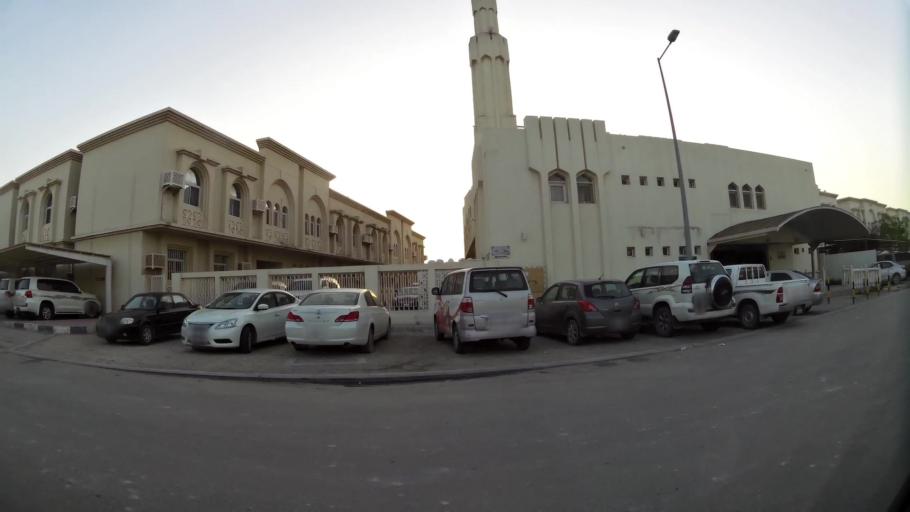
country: QA
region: Baladiyat ar Rayyan
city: Ar Rayyan
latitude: 25.3211
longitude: 51.4655
